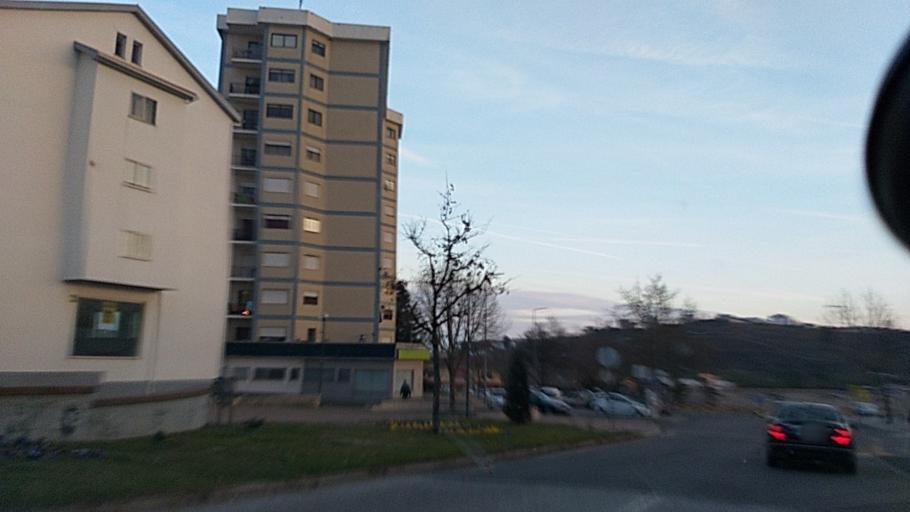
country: PT
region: Guarda
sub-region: Guarda
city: Sequeira
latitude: 40.5513
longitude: -7.2463
